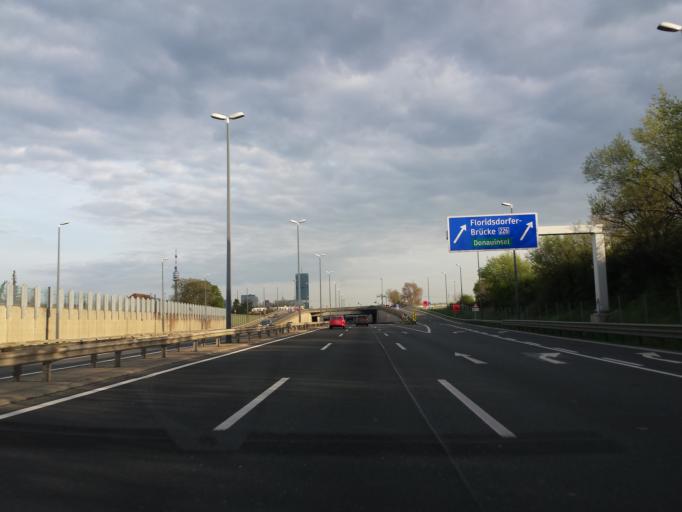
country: AT
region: Vienna
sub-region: Wien Stadt
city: Vienna
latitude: 48.2528
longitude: 16.3887
